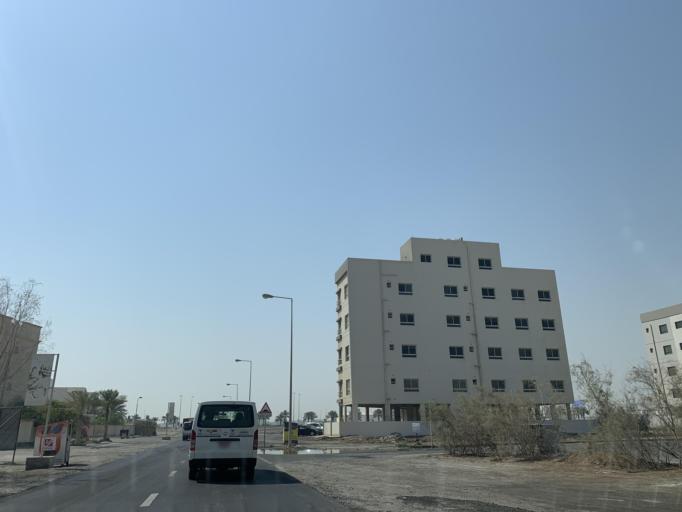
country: BH
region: Northern
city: Madinat `Isa
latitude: 26.1945
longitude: 50.5151
